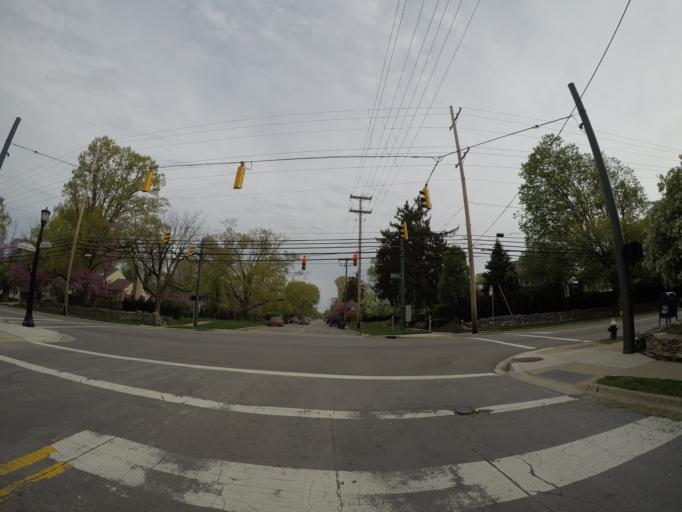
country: US
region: Ohio
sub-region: Franklin County
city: Upper Arlington
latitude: 39.9893
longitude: -83.0601
